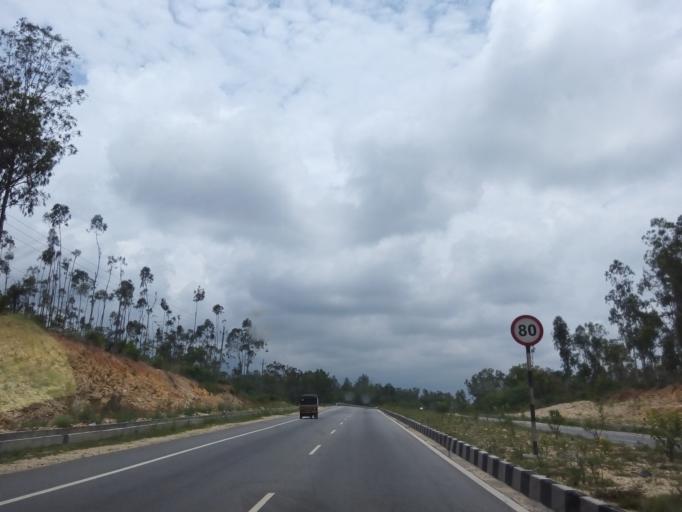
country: IN
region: Karnataka
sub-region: Hassan
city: Hassan
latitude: 12.9924
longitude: 76.1777
